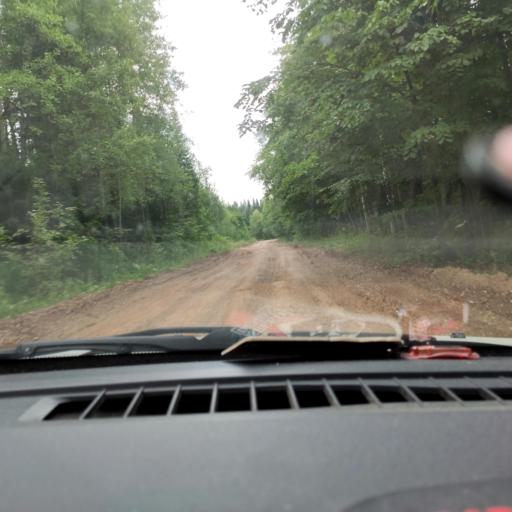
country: RU
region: Perm
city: Kultayevo
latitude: 57.8090
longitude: 56.0038
